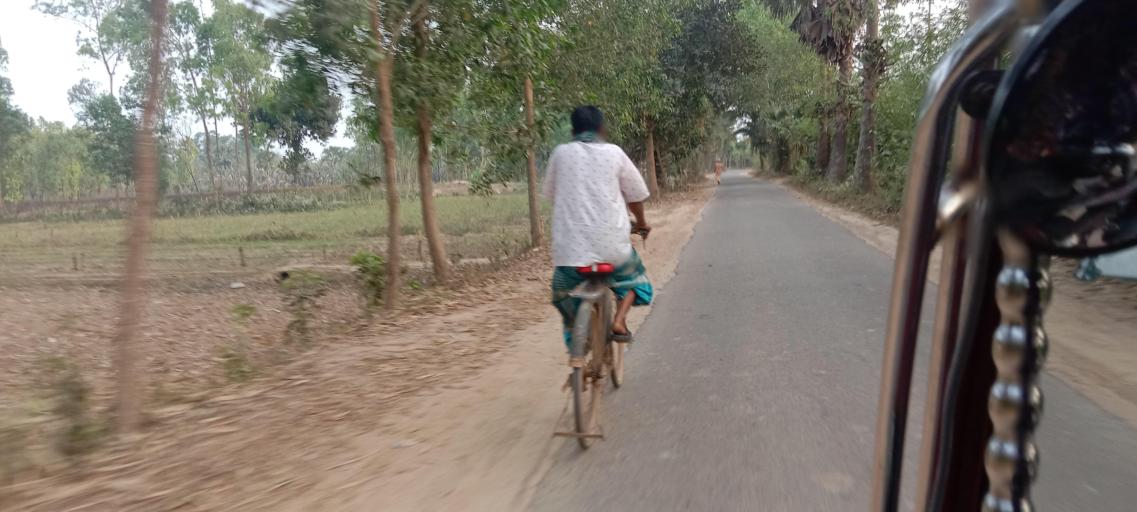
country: BD
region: Dhaka
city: Sakhipur
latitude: 24.4343
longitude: 90.2629
